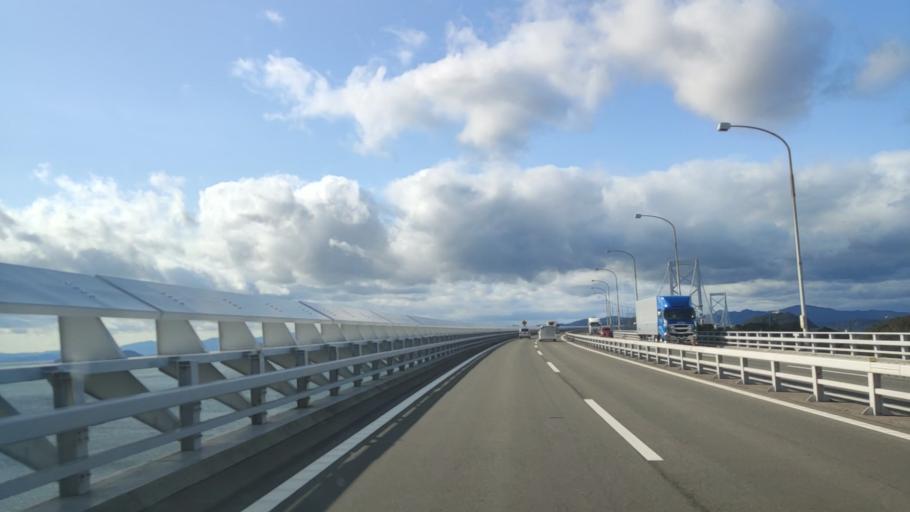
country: JP
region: Hyogo
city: Fukura
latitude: 34.2441
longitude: 134.6658
